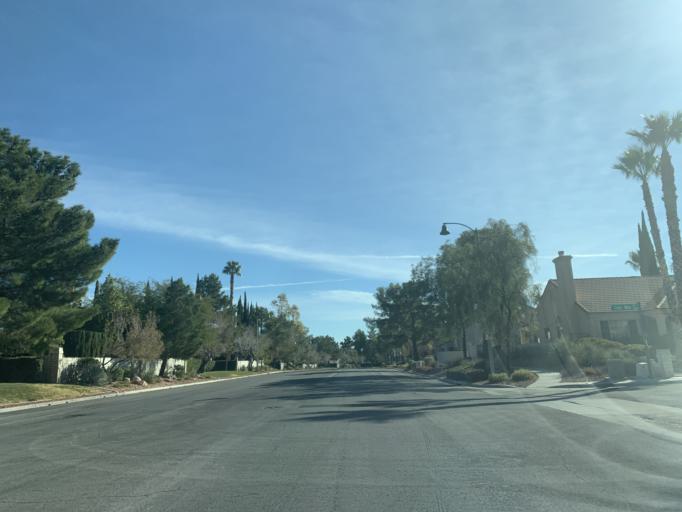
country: US
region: Nevada
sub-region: Clark County
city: Summerlin South
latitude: 36.1318
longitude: -115.2902
